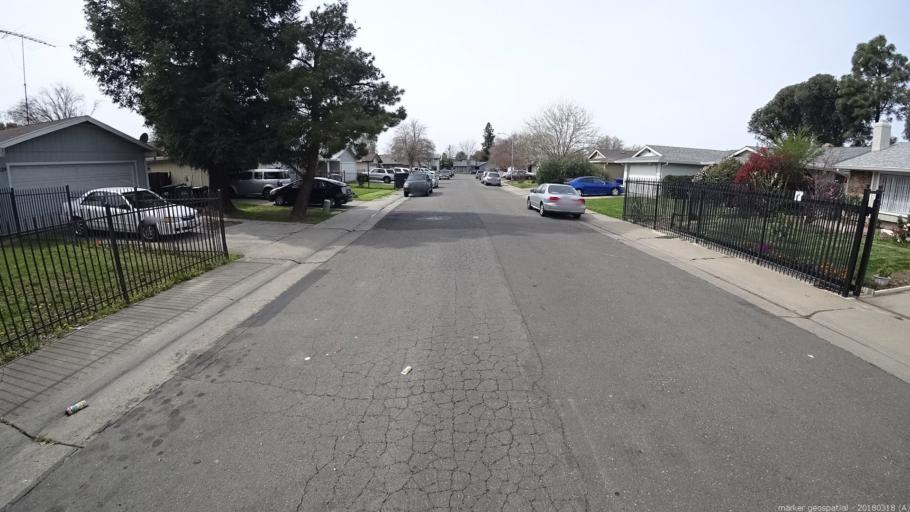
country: US
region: California
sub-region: Sacramento County
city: Parkway
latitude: 38.5166
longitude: -121.4464
